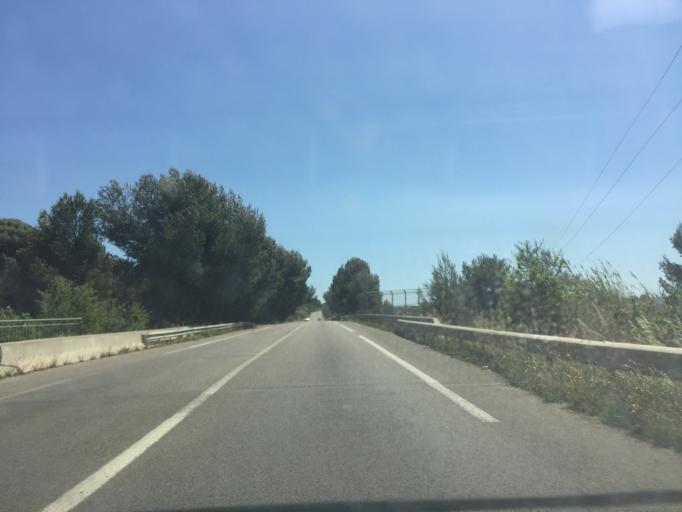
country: FR
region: Provence-Alpes-Cote d'Azur
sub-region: Departement des Bouches-du-Rhone
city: Vitrolles
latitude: 43.4553
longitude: 5.2351
